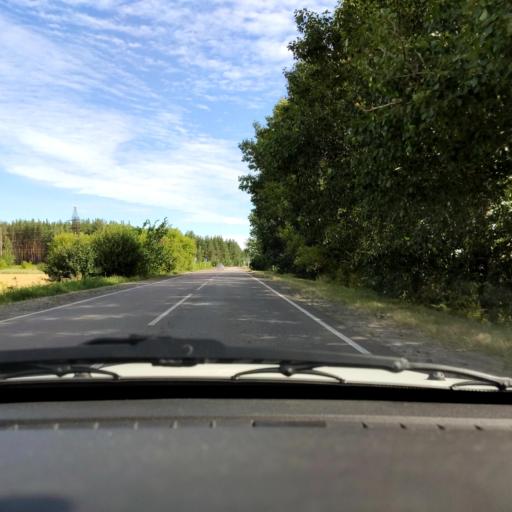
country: RU
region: Voronezj
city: Uglyanets
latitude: 51.8484
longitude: 39.6587
